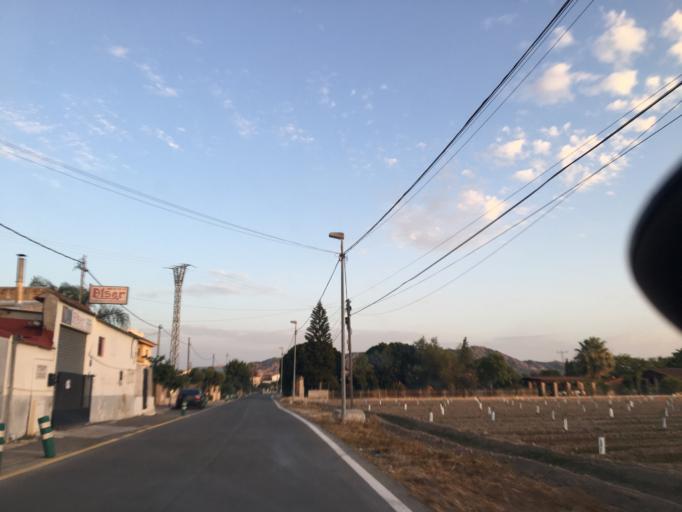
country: ES
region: Murcia
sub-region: Murcia
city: Santomera
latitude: 38.0239
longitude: -1.0551
